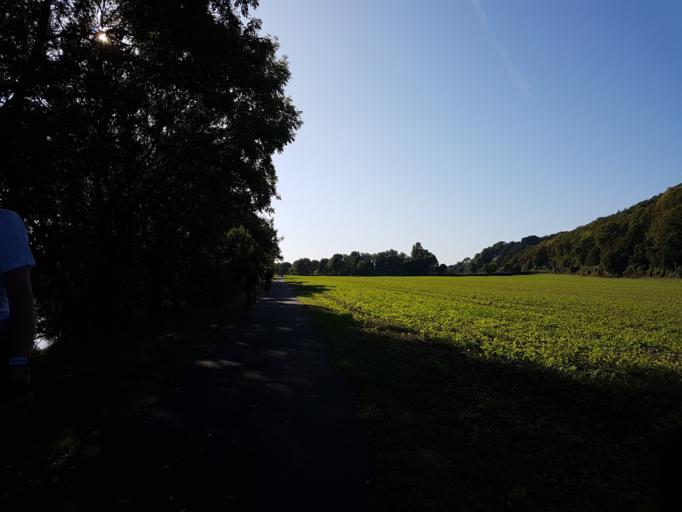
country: DE
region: North Rhine-Westphalia
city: Porta Westfalica
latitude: 52.2405
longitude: 8.9013
